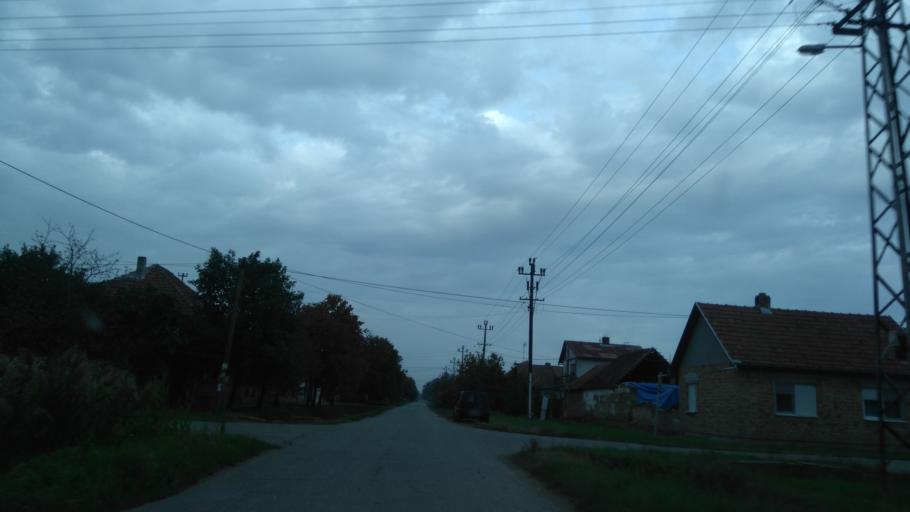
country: RS
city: Mol
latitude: 45.7606
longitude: 20.1367
